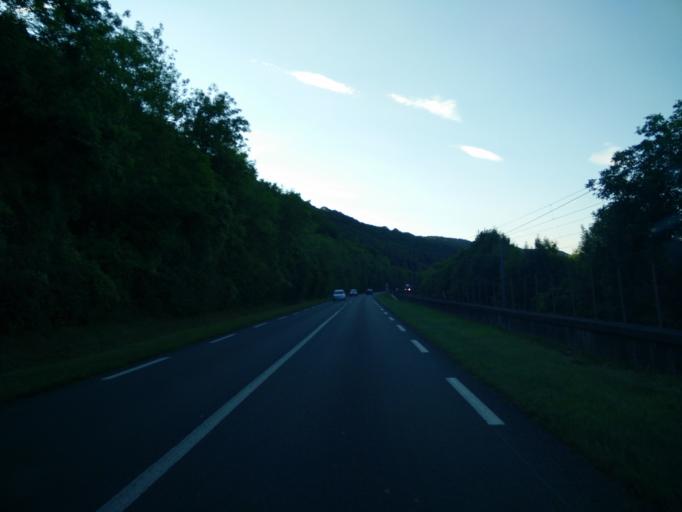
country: FR
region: Ile-de-France
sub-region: Departement des Yvelines
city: Bennecourt
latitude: 49.0373
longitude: 1.5414
